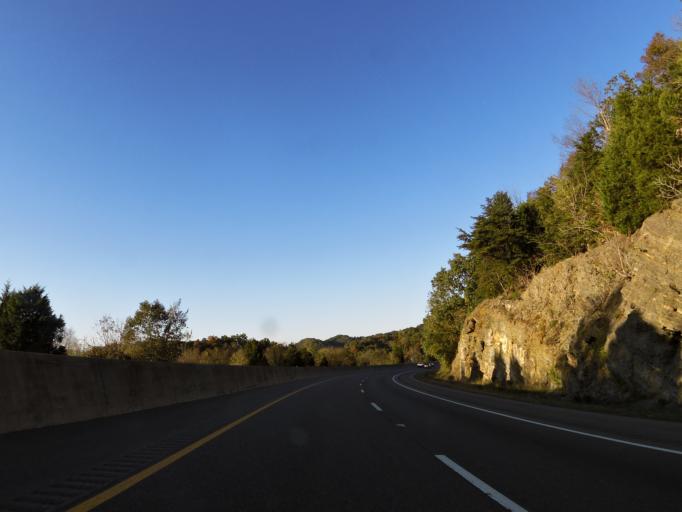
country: US
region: Tennessee
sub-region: Anderson County
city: Clinton
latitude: 36.0811
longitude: -84.0187
